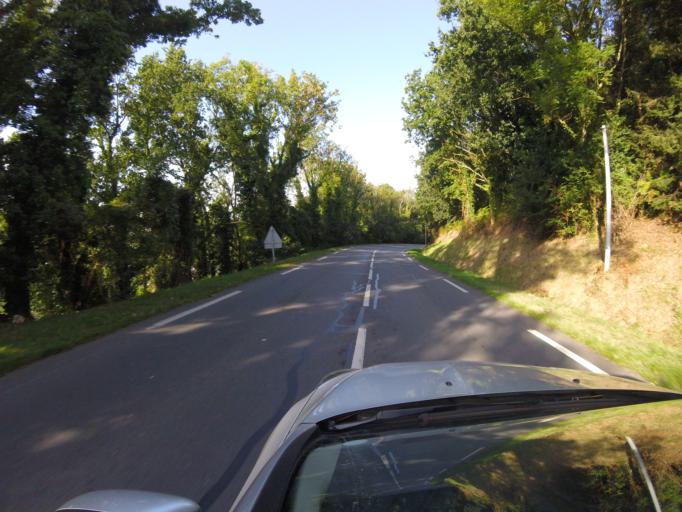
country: FR
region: Haute-Normandie
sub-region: Departement de la Seine-Maritime
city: Fecamp
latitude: 49.7624
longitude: 0.3987
